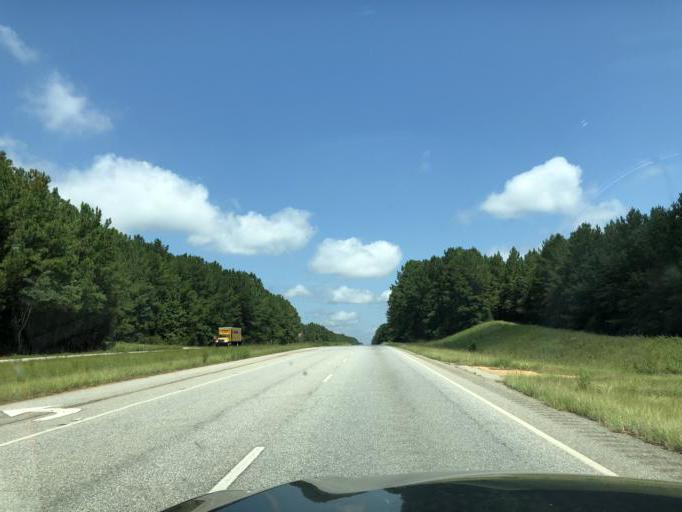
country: US
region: Alabama
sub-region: Henry County
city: Abbeville
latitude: 31.6536
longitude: -85.2802
